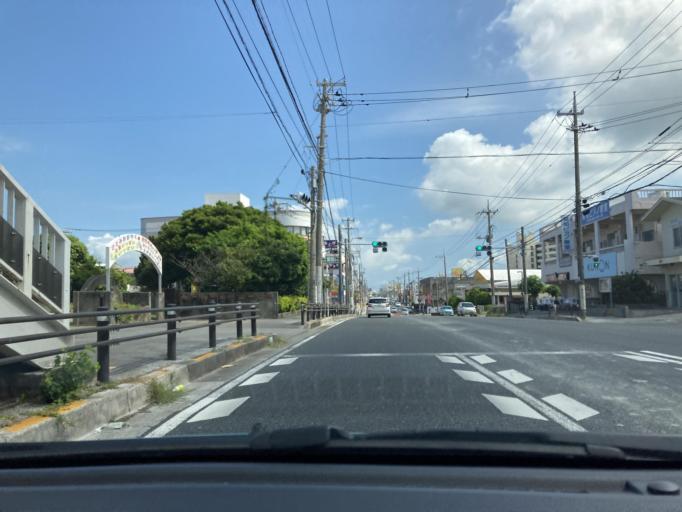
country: JP
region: Okinawa
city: Ginowan
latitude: 26.2684
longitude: 127.7674
